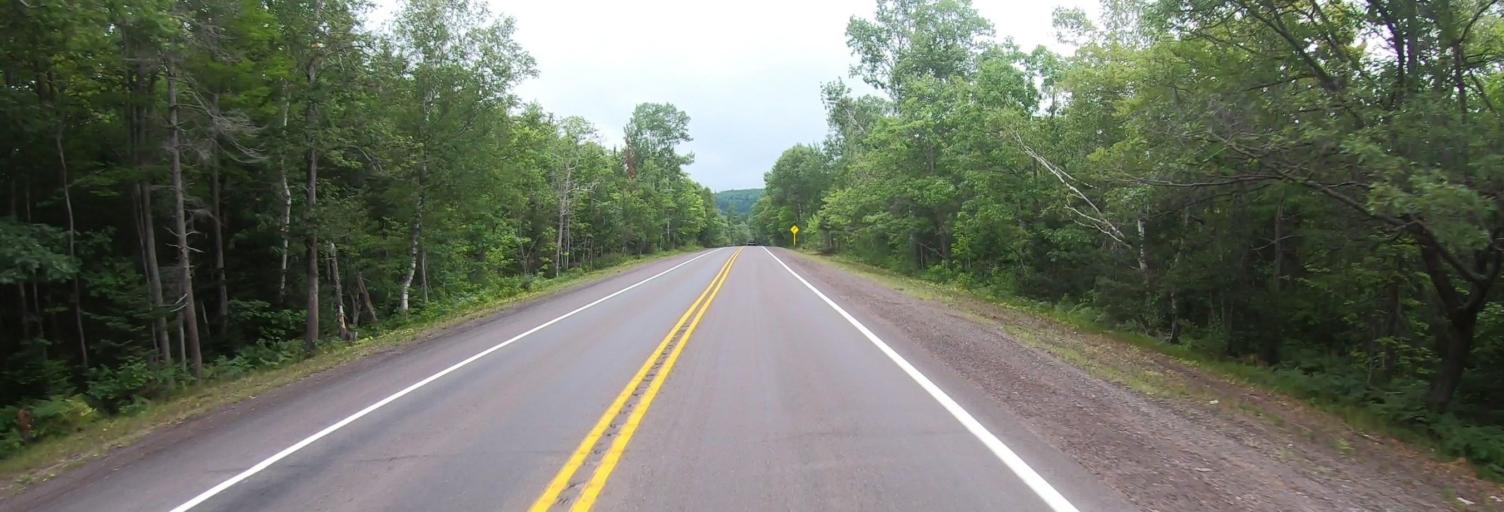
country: US
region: Michigan
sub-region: Keweenaw County
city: Eagle River
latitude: 47.3628
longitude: -88.3037
